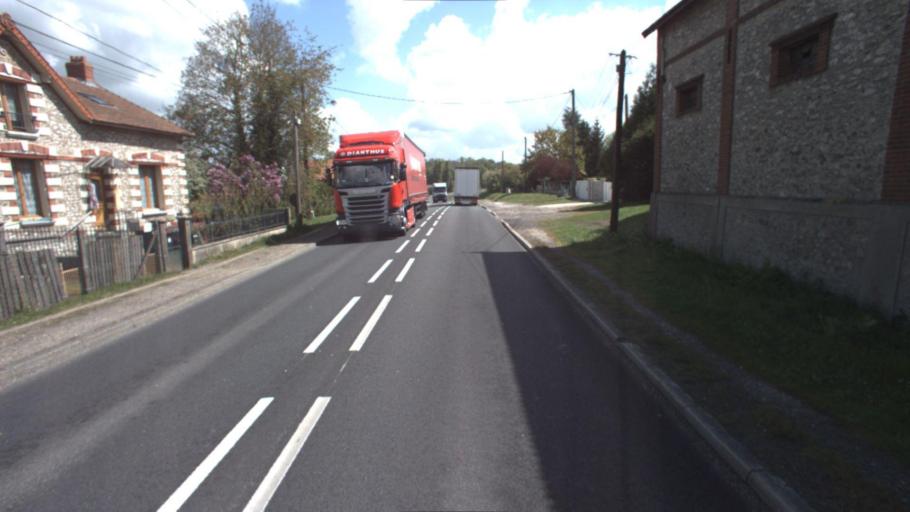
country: FR
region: Ile-de-France
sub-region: Departement de Seine-et-Marne
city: Choisy-en-Brie
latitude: 48.6999
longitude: 3.2461
